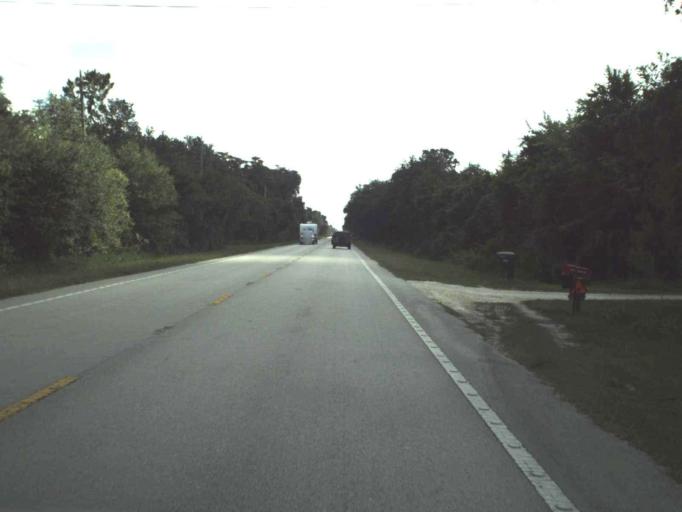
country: US
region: Florida
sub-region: Volusia County
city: Samsula-Spruce Creek
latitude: 28.9291
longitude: -81.1122
